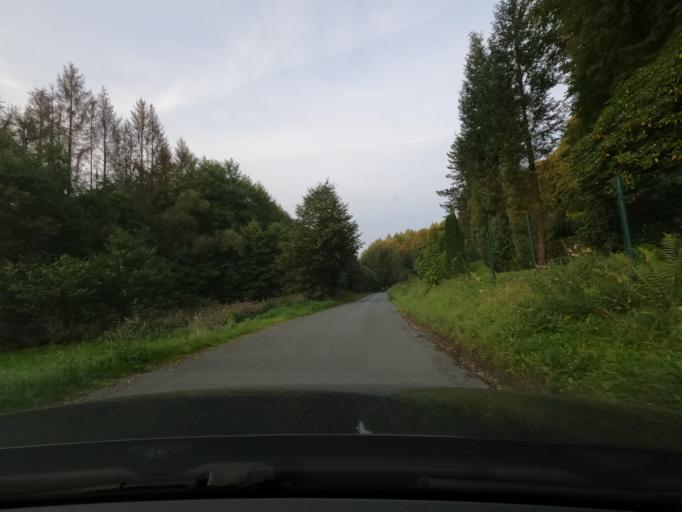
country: DE
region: North Rhine-Westphalia
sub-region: Regierungsbezirk Arnsberg
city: Luedenscheid
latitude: 51.2172
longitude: 7.6884
